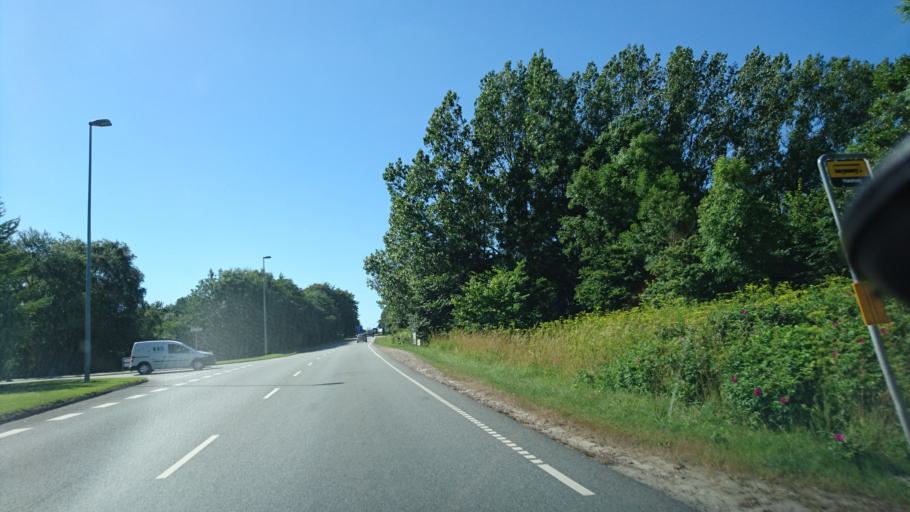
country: DK
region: North Denmark
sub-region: Alborg Kommune
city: Gistrup
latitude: 57.0427
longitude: 9.9790
